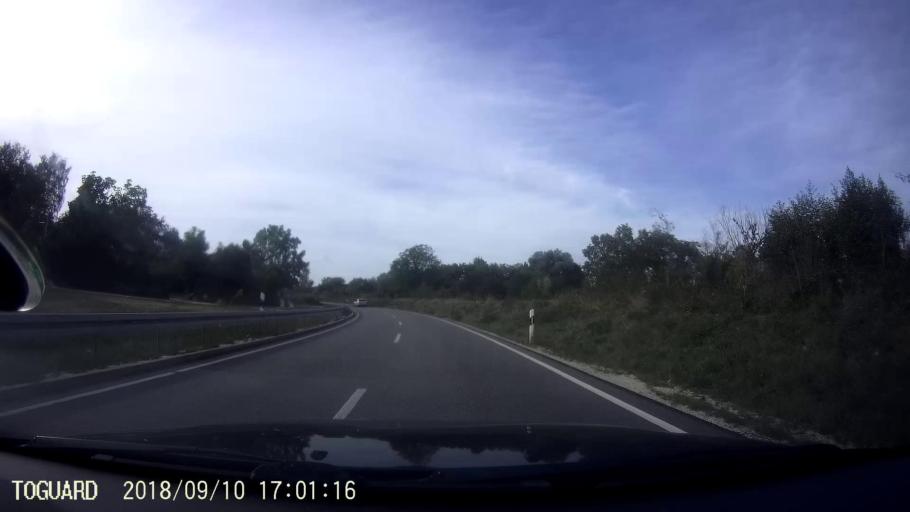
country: CH
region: Thurgau
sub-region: Kreuzlingen District
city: Gottlieben
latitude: 47.6932
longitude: 9.1363
